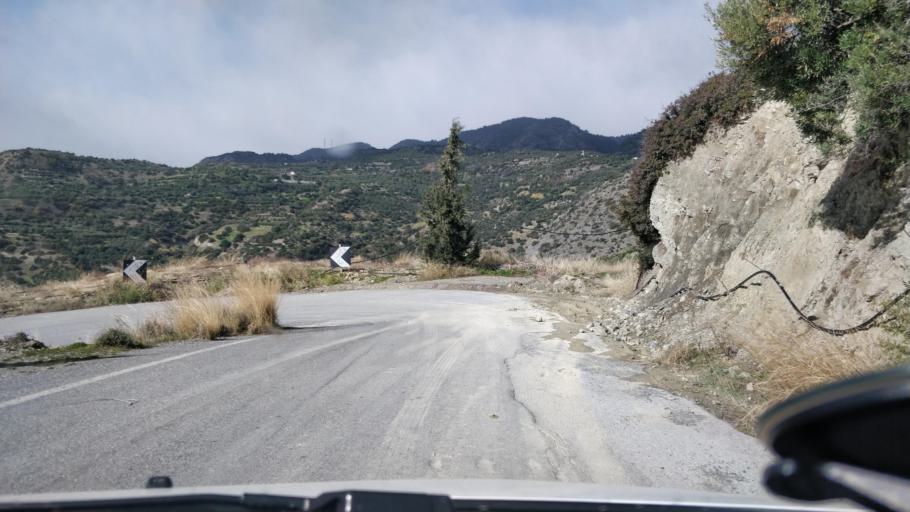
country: GR
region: Crete
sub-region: Nomos Lasithiou
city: Gra Liyia
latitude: 35.0036
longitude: 25.5002
